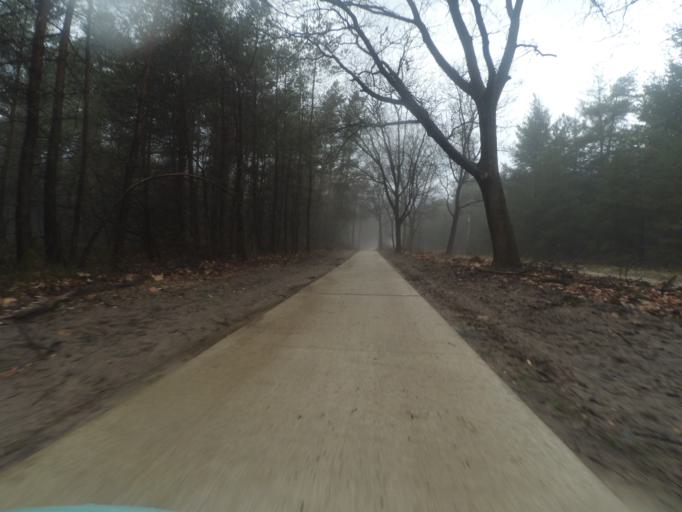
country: NL
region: Gelderland
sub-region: Gemeente Apeldoorn
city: Beekbergen
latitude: 52.1352
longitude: 5.9098
